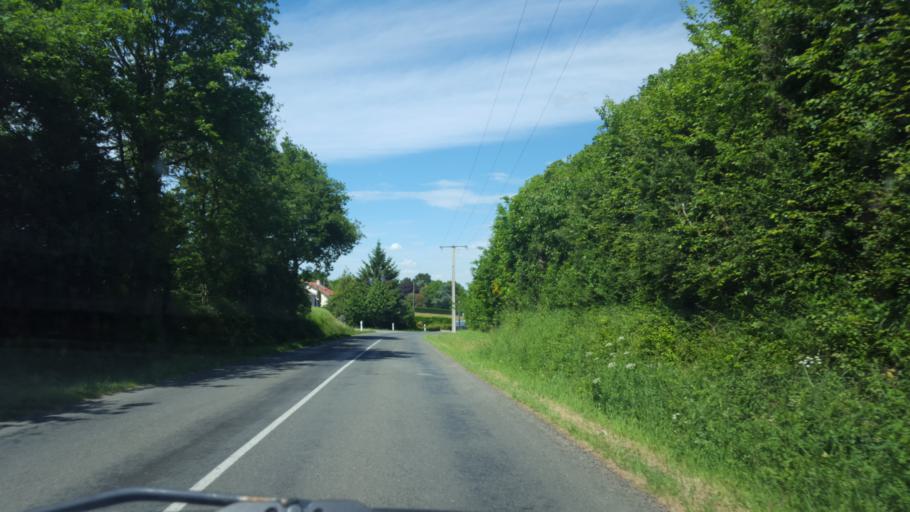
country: FR
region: Pays de la Loire
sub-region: Departement de la Loire-Atlantique
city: Saint-Philbert-de-Grand-Lieu
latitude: 47.0238
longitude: -1.6450
